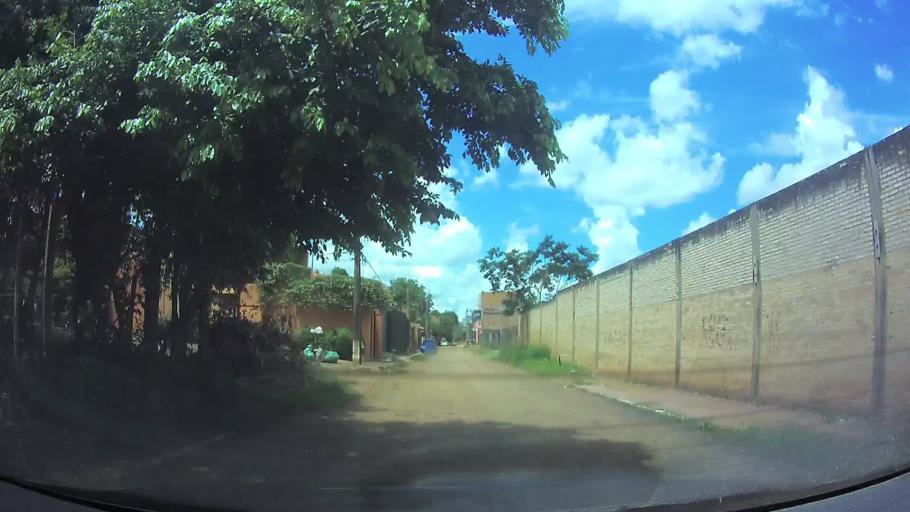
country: PY
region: Central
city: Fernando de la Mora
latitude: -25.3156
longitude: -57.5253
